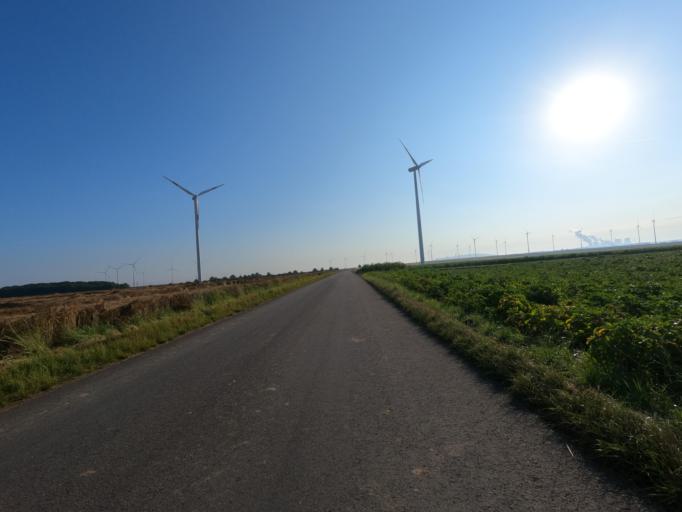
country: DE
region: North Rhine-Westphalia
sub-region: Regierungsbezirk Koln
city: Titz
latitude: 51.0269
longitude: 6.4890
